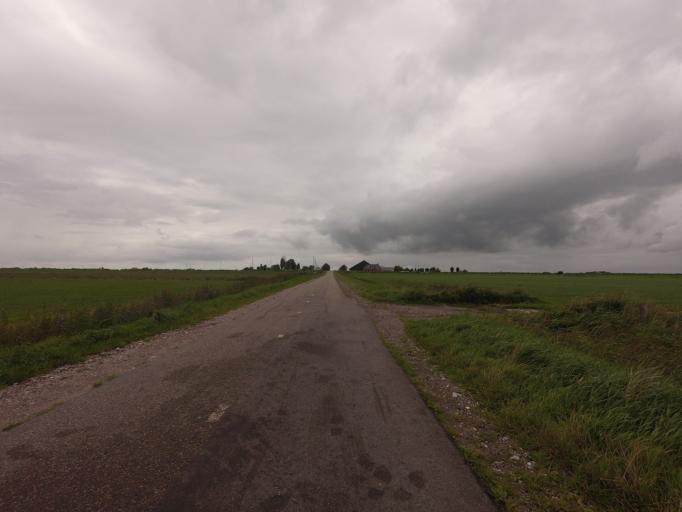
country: NL
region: Friesland
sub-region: Sudwest Fryslan
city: Workum
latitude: 52.9722
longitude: 5.5218
